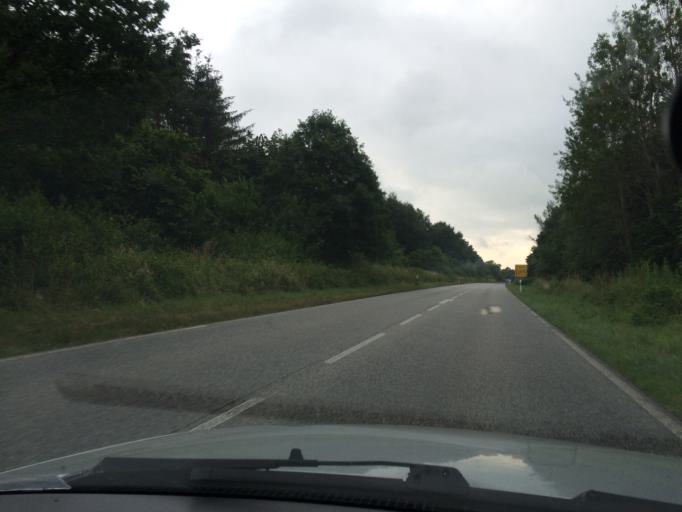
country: DE
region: Schleswig-Holstein
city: Sieverstedt
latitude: 54.6439
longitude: 9.4582
